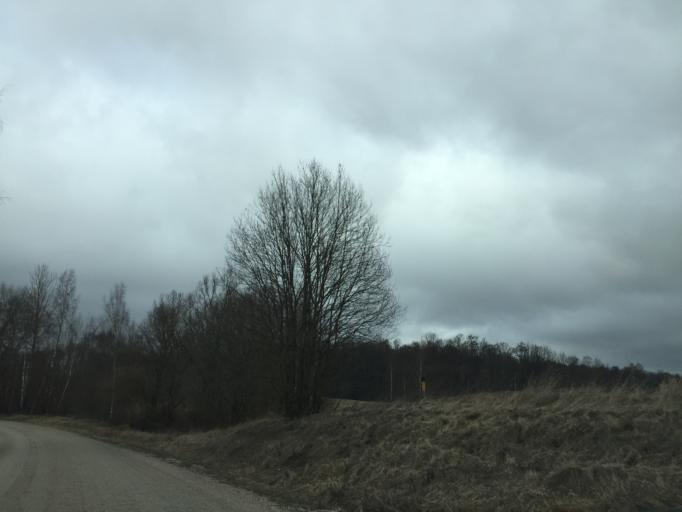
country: LV
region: Ilukste
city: Ilukste
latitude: 56.0162
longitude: 26.2632
